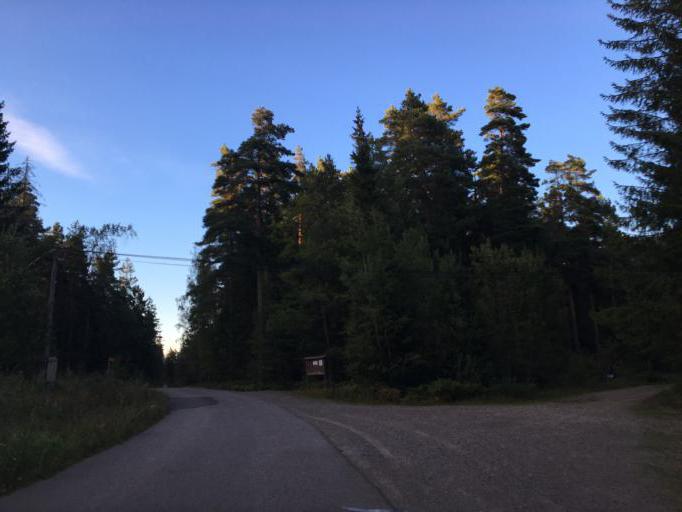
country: SE
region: Soedermanland
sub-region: Eskilstuna Kommun
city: Hallbybrunn
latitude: 59.4262
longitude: 16.4301
